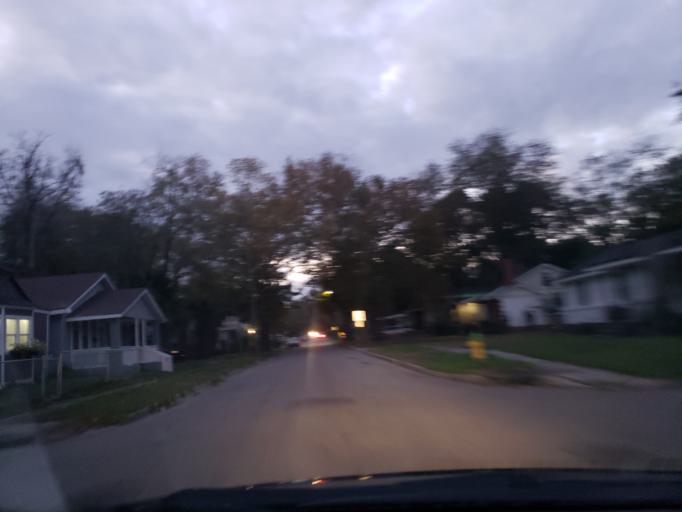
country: US
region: Georgia
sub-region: Chatham County
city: Thunderbolt
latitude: 32.0487
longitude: -81.0810
